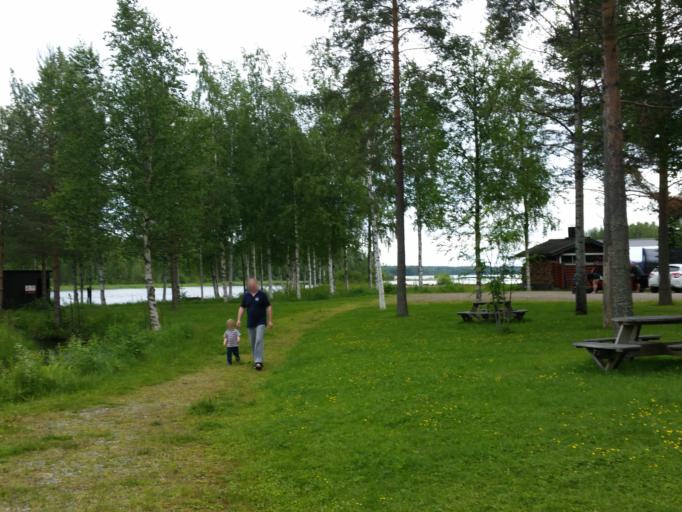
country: FI
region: Northern Savo
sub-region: Sisae-Savo
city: Tervo
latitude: 63.0065
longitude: 26.6881
